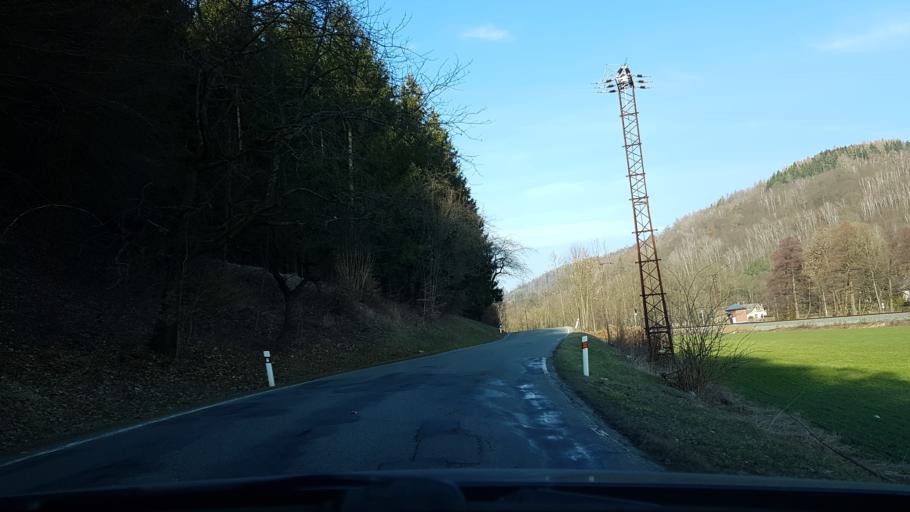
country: CZ
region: Olomoucky
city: Dolni Bohdikov
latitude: 50.0146
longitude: 16.8969
